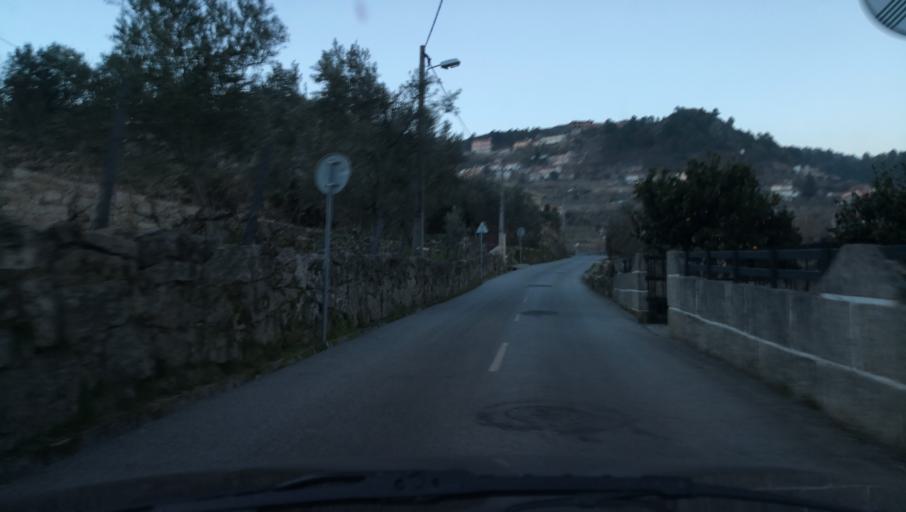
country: PT
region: Vila Real
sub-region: Vila Real
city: Vila Real
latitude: 41.3163
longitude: -7.7871
